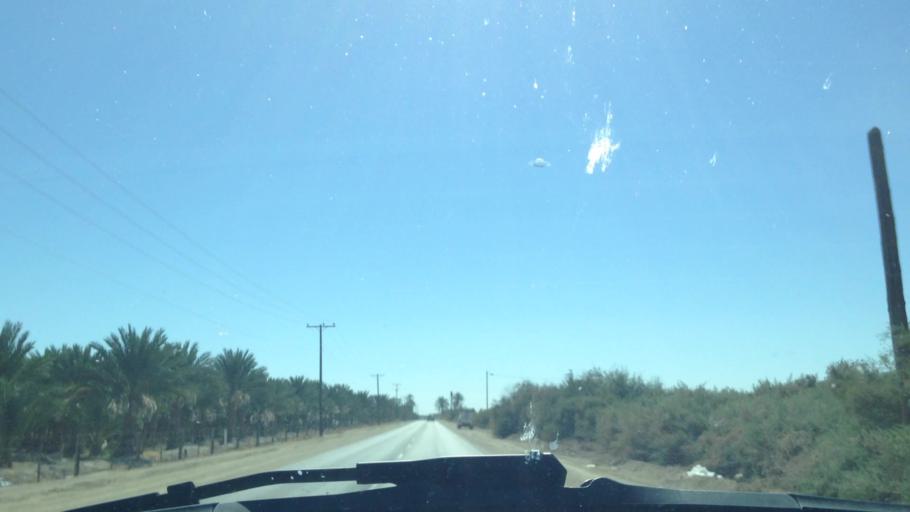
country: US
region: California
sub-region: Riverside County
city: Mecca
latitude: 33.5446
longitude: -116.0385
